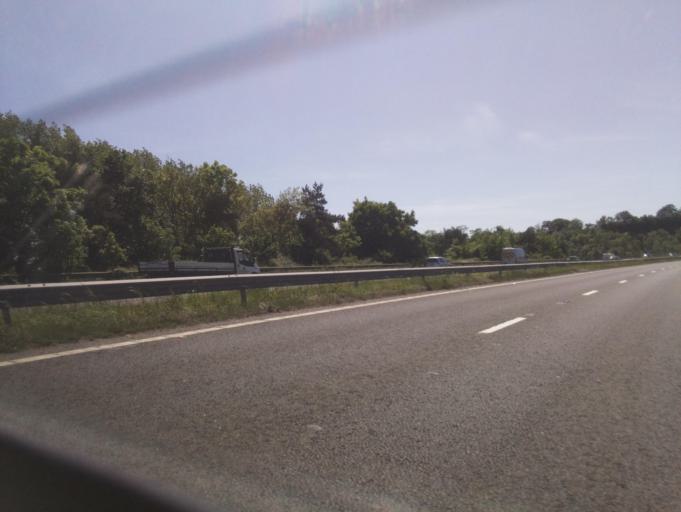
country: GB
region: England
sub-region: Devon
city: Exminster
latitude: 50.6863
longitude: -3.4908
